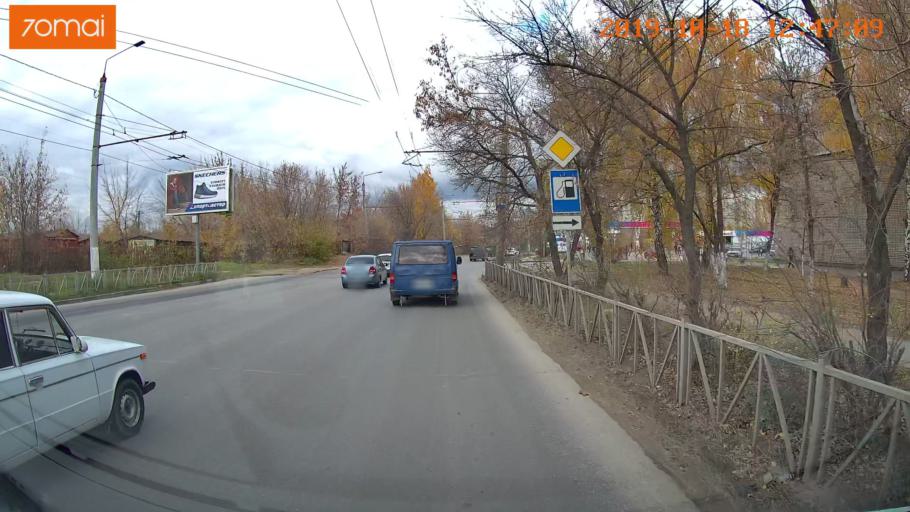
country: RU
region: Rjazan
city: Ryazan'
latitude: 54.6569
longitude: 39.6634
